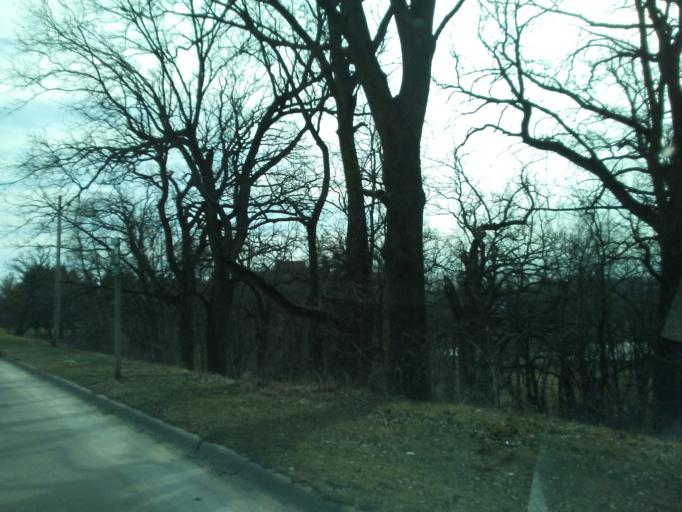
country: US
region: Iowa
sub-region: Winneshiek County
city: Decorah
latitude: 43.3187
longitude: -91.8045
